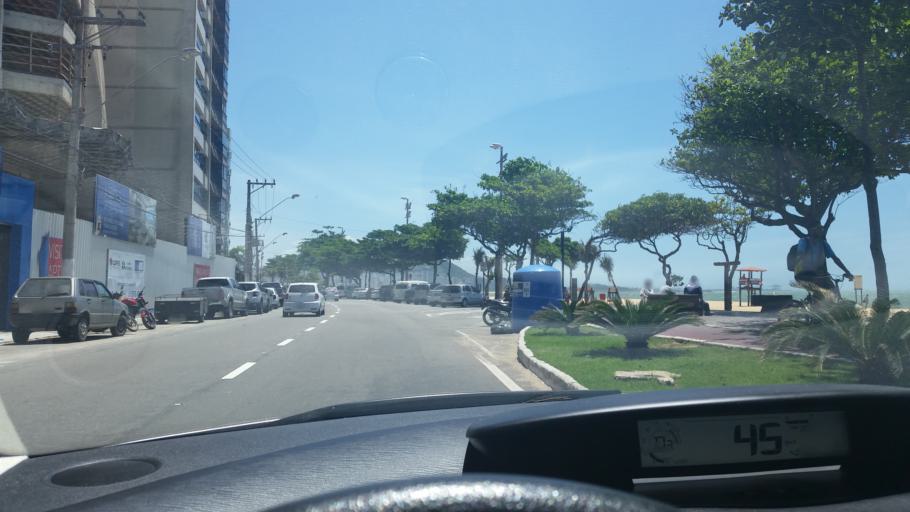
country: BR
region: Espirito Santo
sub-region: Vila Velha
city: Vila Velha
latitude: -20.3522
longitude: -40.2839
